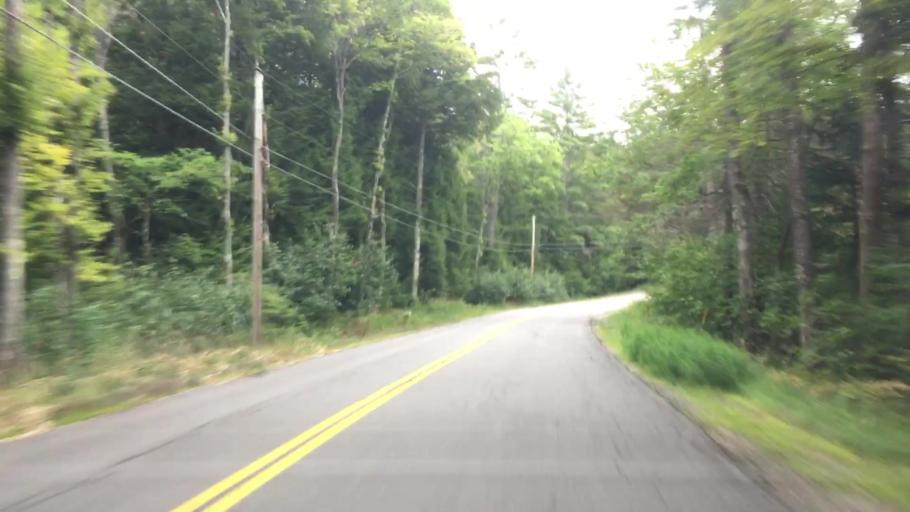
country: US
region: Maine
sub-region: Cumberland County
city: New Gloucester
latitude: 43.9054
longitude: -70.2133
